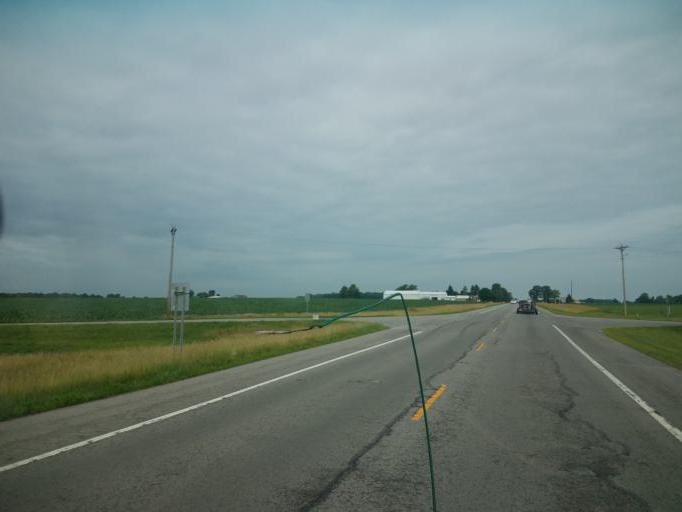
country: US
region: Ohio
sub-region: Hardin County
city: Kenton
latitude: 40.6780
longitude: -83.6728
